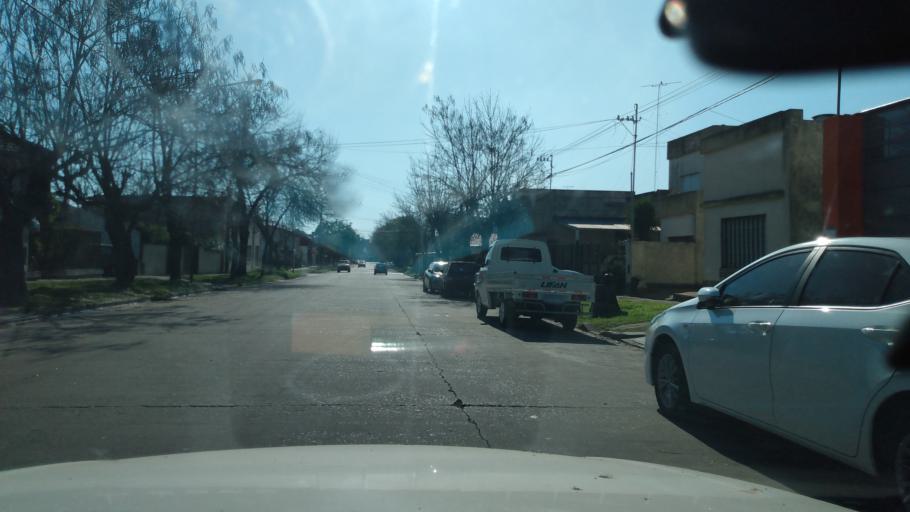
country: AR
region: Buenos Aires
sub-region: Partido de Lujan
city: Lujan
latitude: -34.5739
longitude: -59.1118
